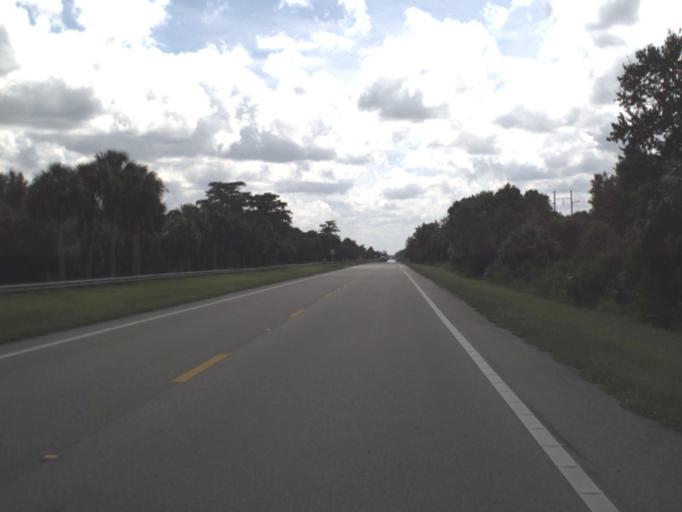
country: US
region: Florida
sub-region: Collier County
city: Immokalee
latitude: 26.3093
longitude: -81.3429
